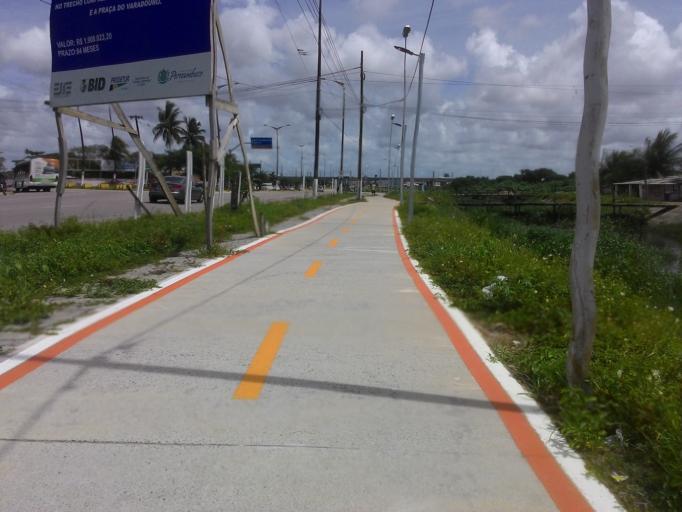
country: BR
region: Pernambuco
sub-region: Olinda
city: Olinda
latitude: -8.0196
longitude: -34.8571
